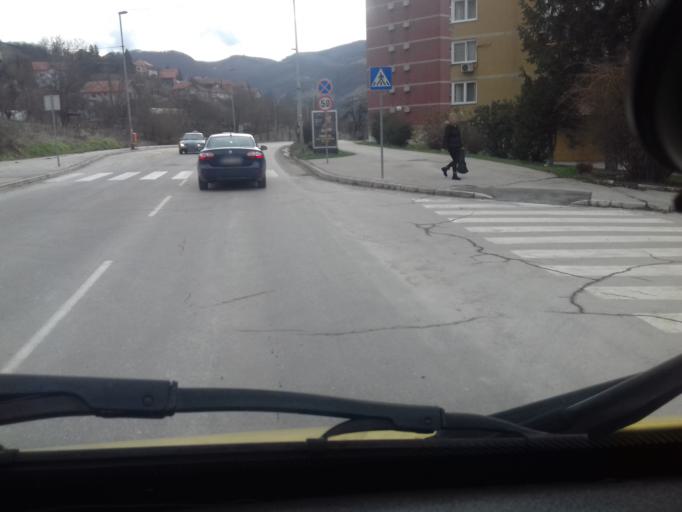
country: BA
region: Federation of Bosnia and Herzegovina
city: Zenica
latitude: 44.2046
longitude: 17.9274
